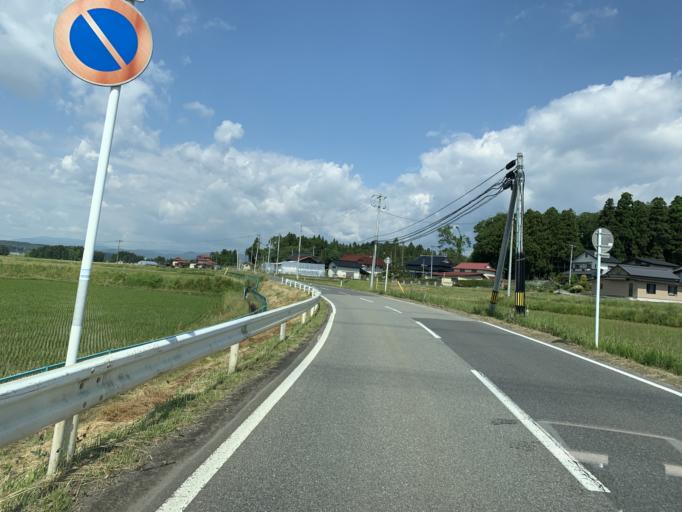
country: JP
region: Iwate
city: Ichinoseki
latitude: 38.8032
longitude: 141.0103
